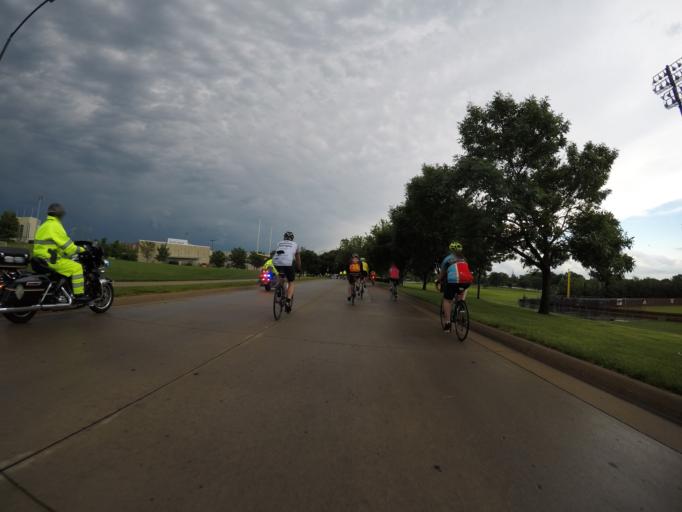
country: US
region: Kansas
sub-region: Shawnee County
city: Topeka
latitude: 39.0317
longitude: -95.7030
